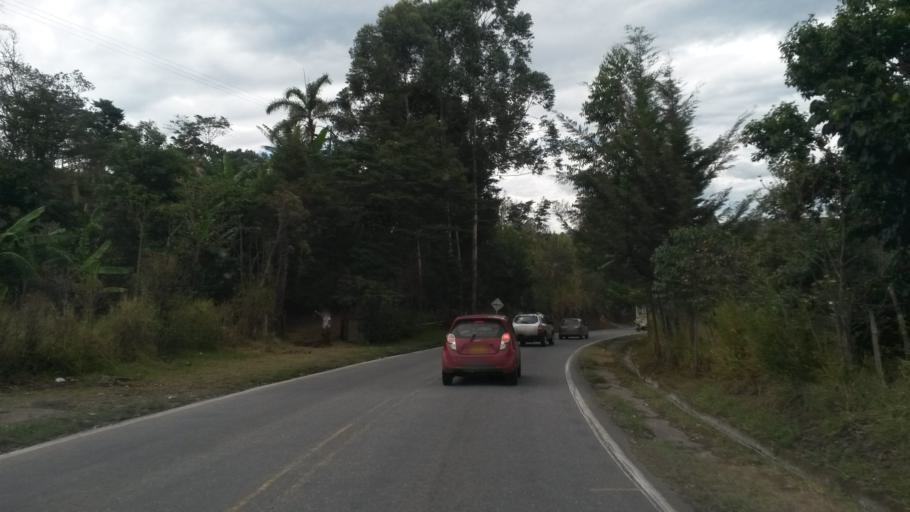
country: CO
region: Cauca
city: Rosas
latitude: 2.3372
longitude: -76.6941
